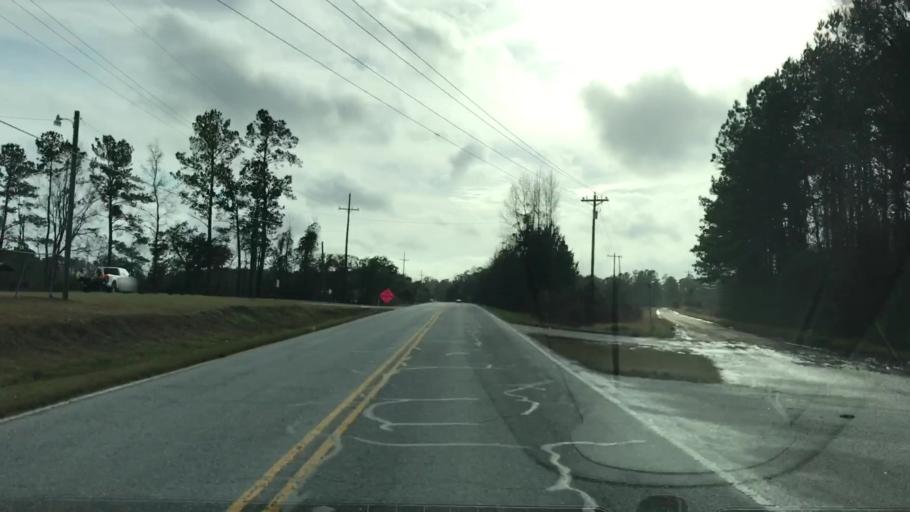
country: US
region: South Carolina
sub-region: Williamsburg County
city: Andrews
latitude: 33.3536
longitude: -79.6589
